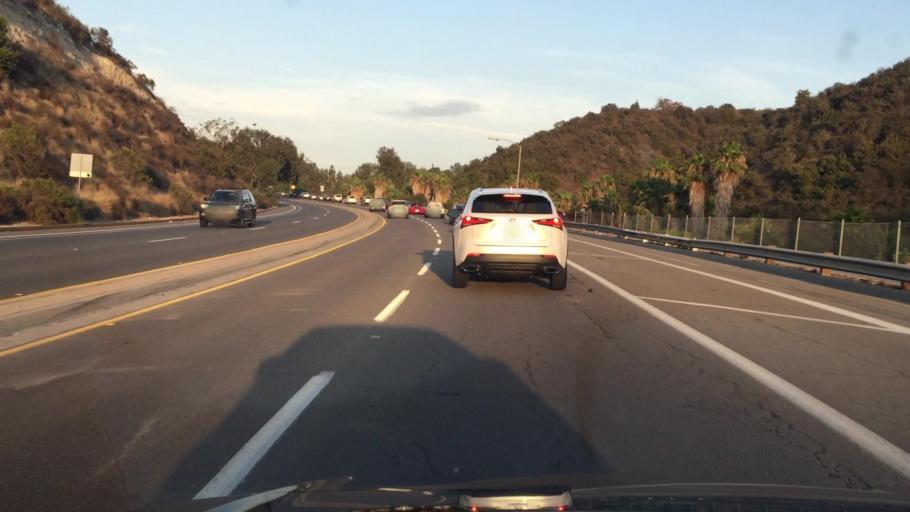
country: US
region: California
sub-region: San Diego County
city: Lemon Grove
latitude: 32.7700
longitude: -117.0915
